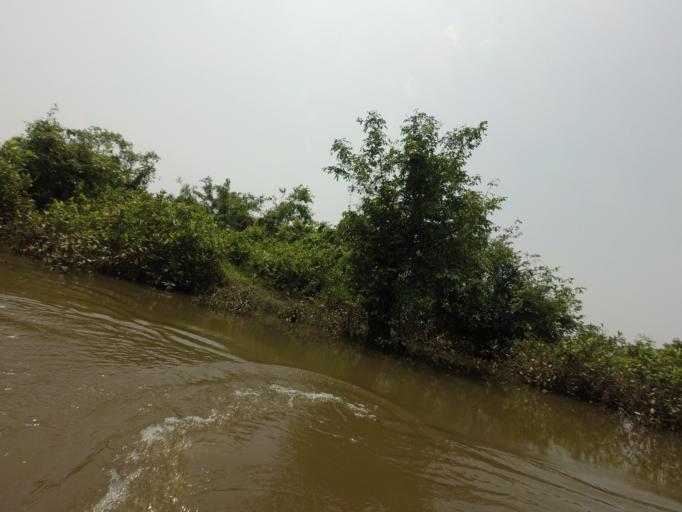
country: BD
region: Sylhet
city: Sylhet
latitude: 25.0132
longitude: 91.9165
